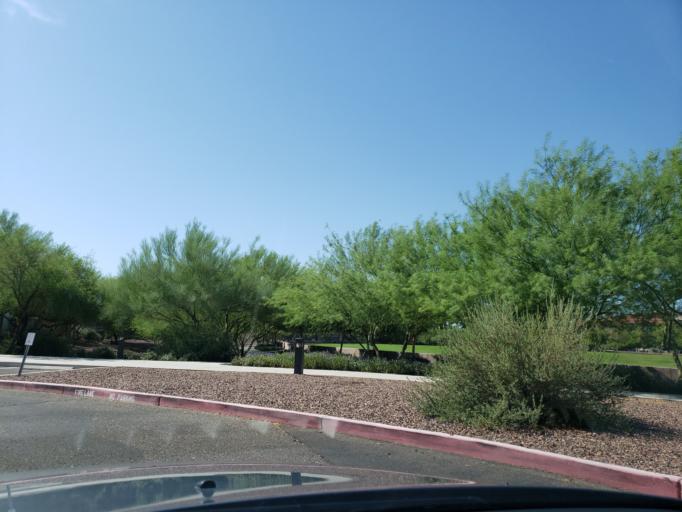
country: US
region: Arizona
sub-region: Maricopa County
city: Peoria
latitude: 33.5753
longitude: -112.2392
